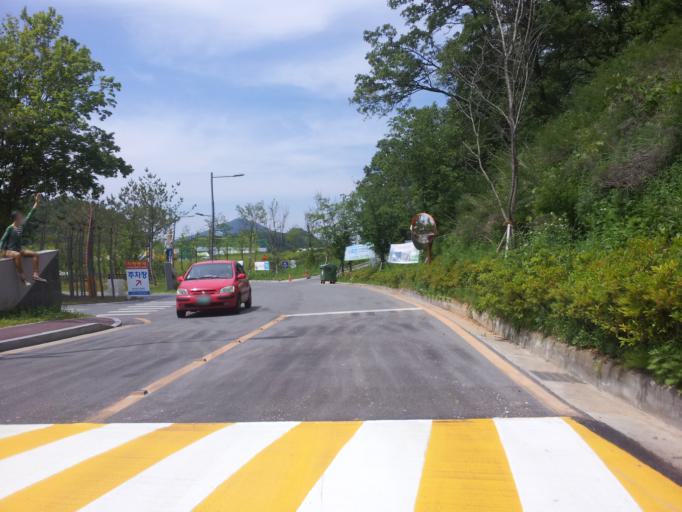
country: KR
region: Daejeon
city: Sintansin
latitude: 36.4562
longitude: 127.4755
